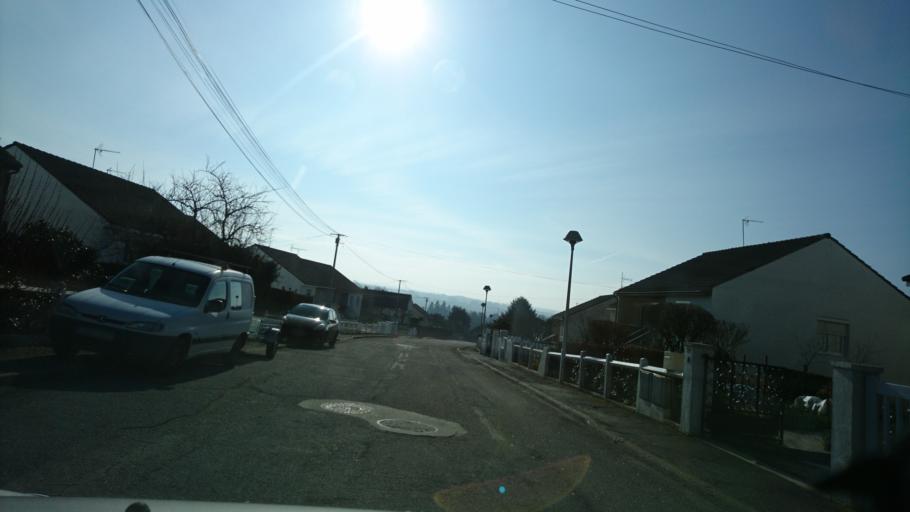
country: FR
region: Limousin
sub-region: Departement de la Haute-Vienne
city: Le Palais-sur-Vienne
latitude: 45.8709
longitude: 1.3148
